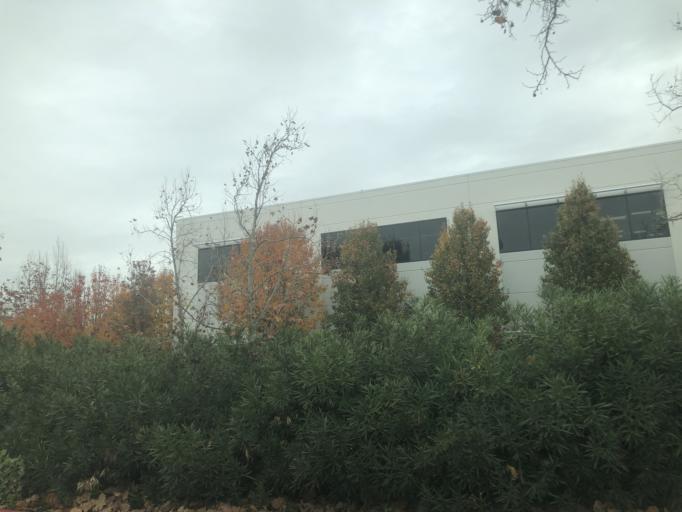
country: US
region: California
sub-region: Santa Clara County
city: Sunnyvale
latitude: 37.3732
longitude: -121.9940
